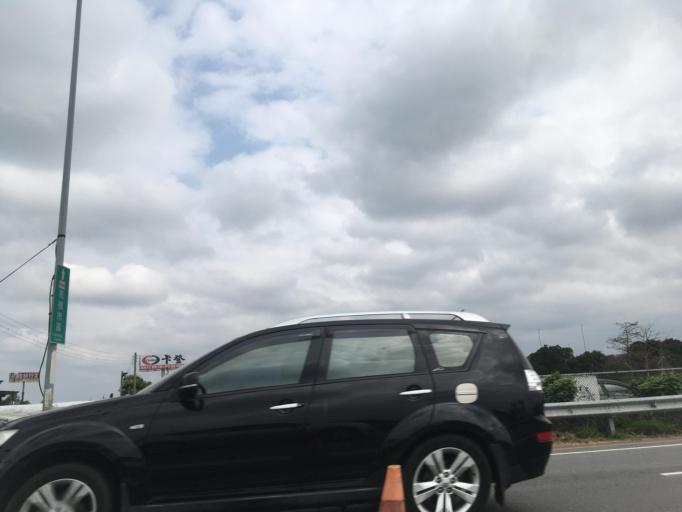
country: TW
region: Taiwan
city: Fengyuan
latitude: 24.3985
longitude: 120.6675
